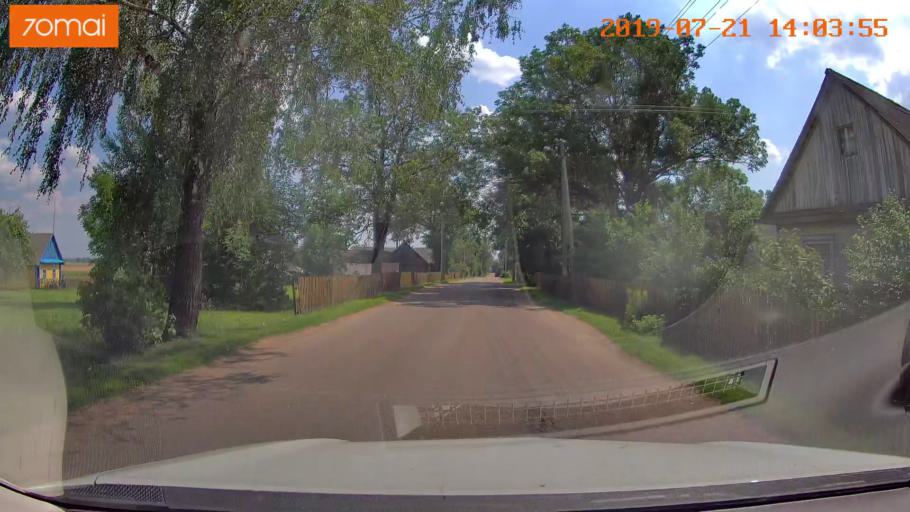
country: BY
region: Grodnenskaya
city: Lyubcha
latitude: 53.7251
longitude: 26.0949
